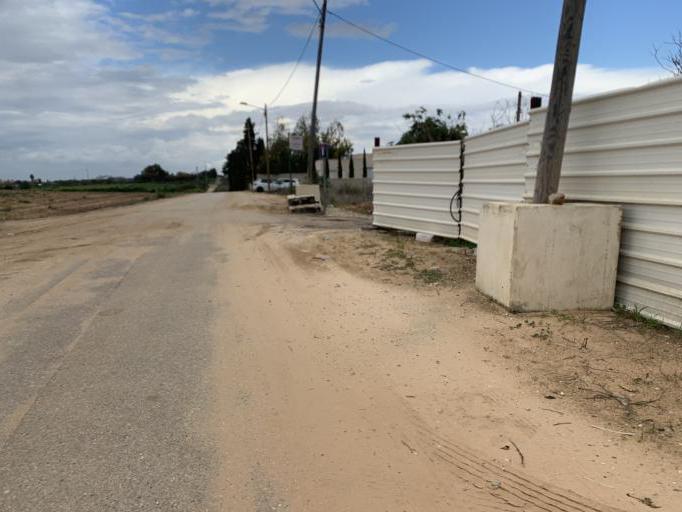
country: IL
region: Central District
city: Hod HaSharon
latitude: 32.1586
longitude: 34.8723
